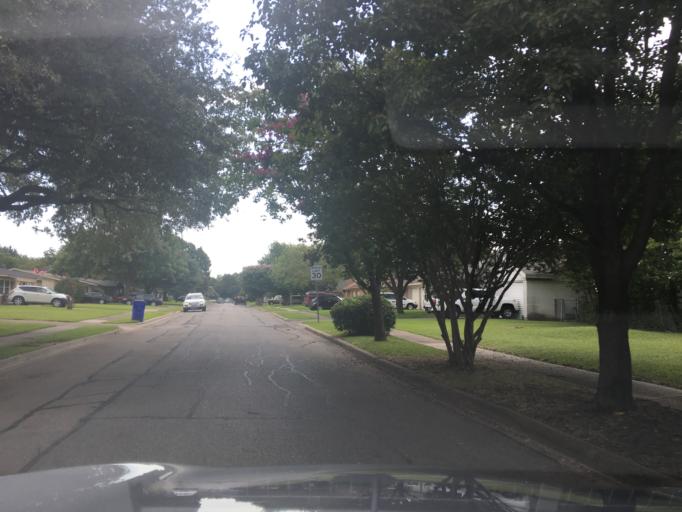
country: US
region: Texas
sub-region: Dallas County
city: Farmers Branch
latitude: 32.9307
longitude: -96.8673
